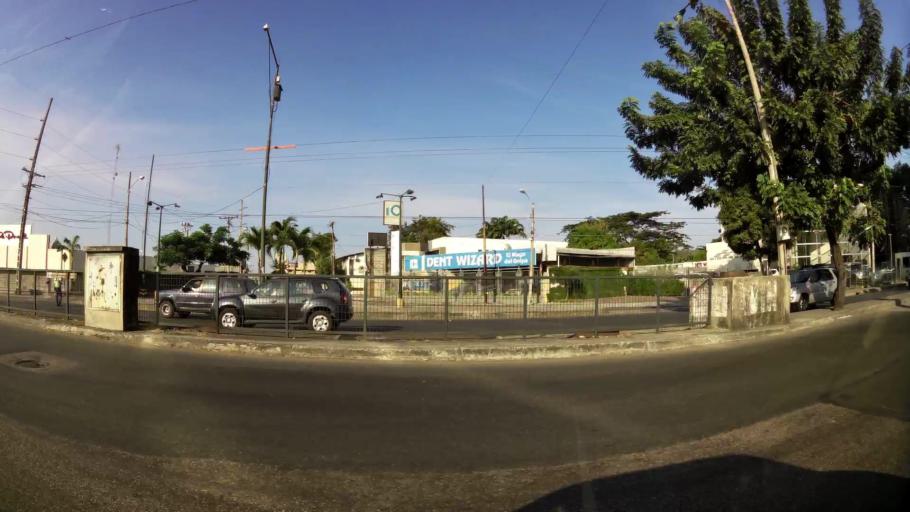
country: EC
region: Guayas
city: Guayaquil
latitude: -2.1690
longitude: -79.9006
